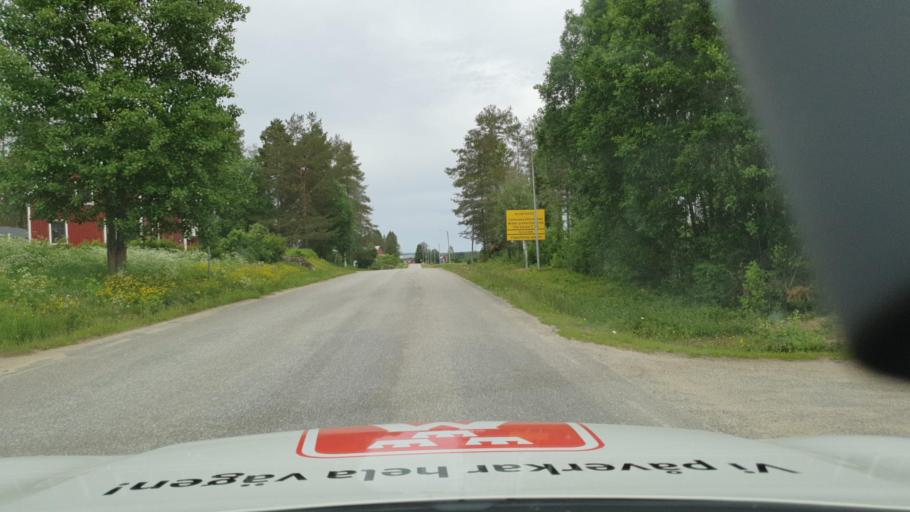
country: SE
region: Vaesterbotten
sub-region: Robertsfors Kommun
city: Robertsfors
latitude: 64.2461
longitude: 20.6609
